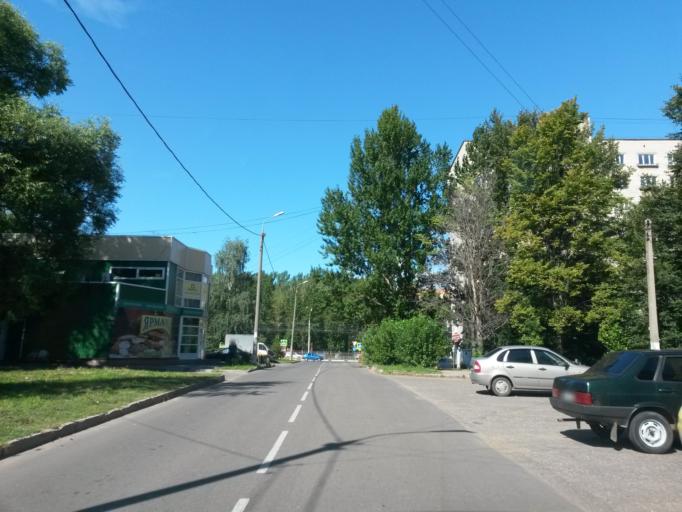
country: RU
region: Jaroslavl
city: Yaroslavl
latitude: 57.5880
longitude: 39.8602
